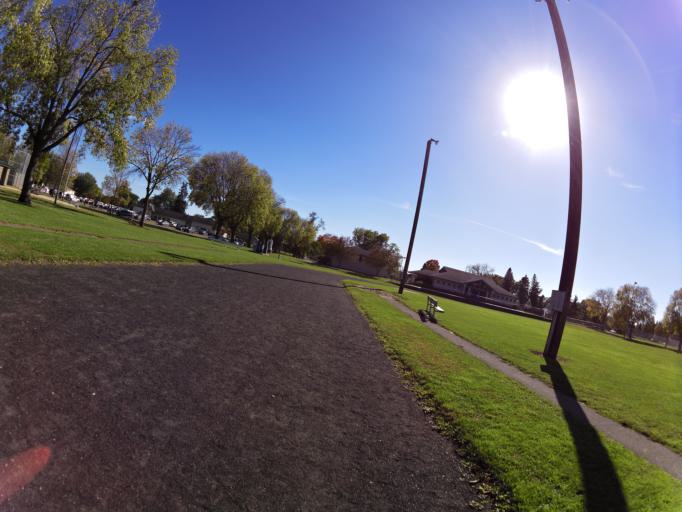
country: US
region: Minnesota
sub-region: Olmsted County
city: Rochester
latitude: 43.9585
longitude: -92.5116
